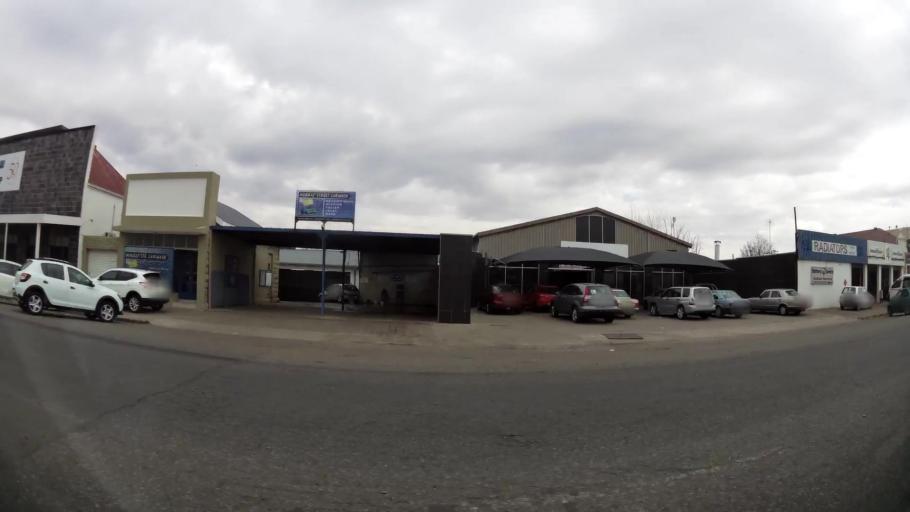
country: ZA
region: Orange Free State
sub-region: Fezile Dabi District Municipality
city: Kroonstad
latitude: -27.6681
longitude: 27.2338
